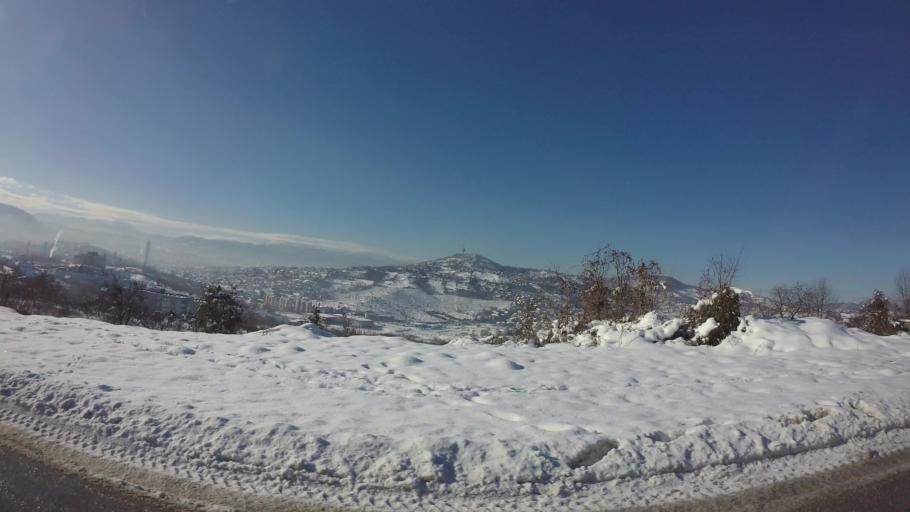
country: BA
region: Federation of Bosnia and Herzegovina
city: Kobilja Glava
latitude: 43.8841
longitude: 18.4100
